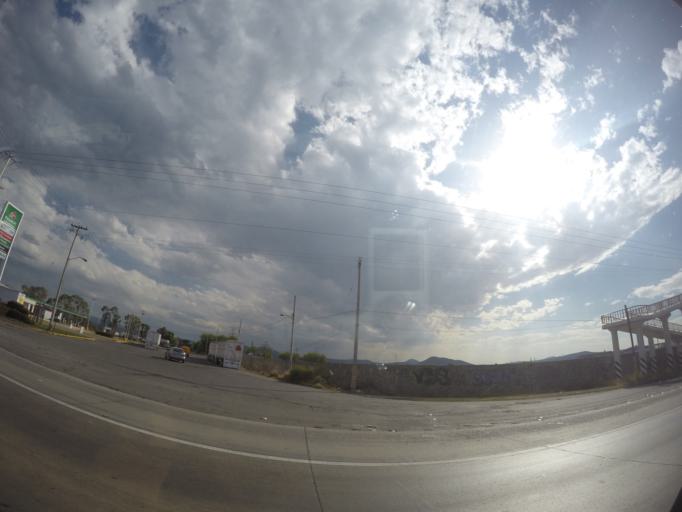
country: MX
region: Queretaro
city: El Sauz
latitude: 20.4849
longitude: -100.1176
